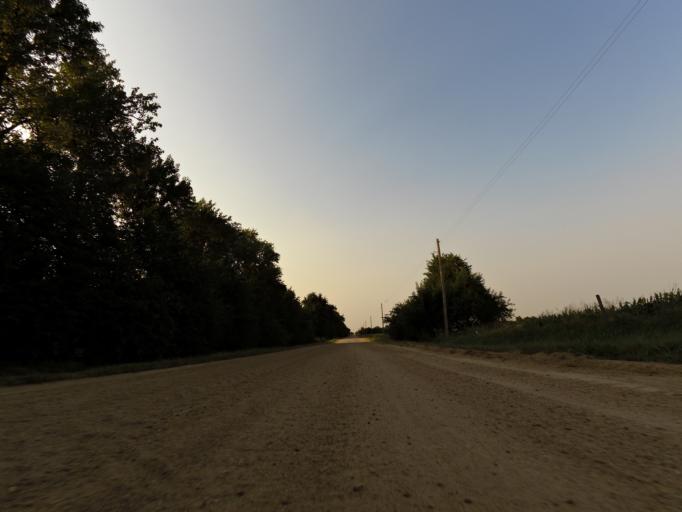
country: US
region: Kansas
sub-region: Reno County
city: South Hutchinson
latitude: 37.9933
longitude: -97.9956
